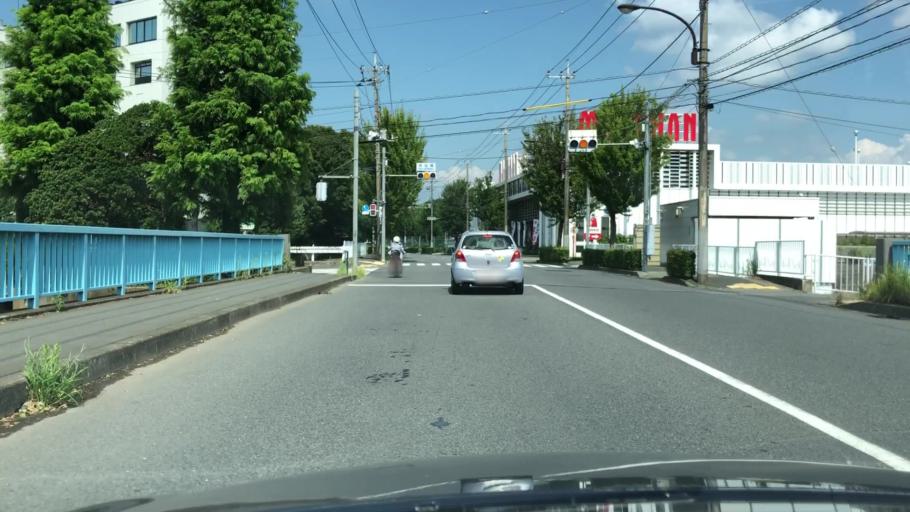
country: JP
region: Tokyo
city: Hino
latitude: 35.6865
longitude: 139.3788
